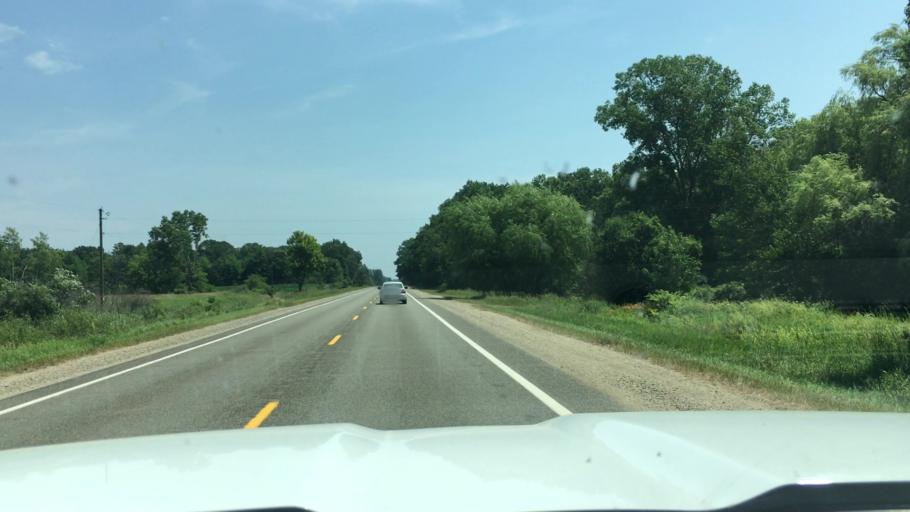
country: US
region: Michigan
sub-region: Clinton County
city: Ovid
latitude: 43.1760
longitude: -84.4005
